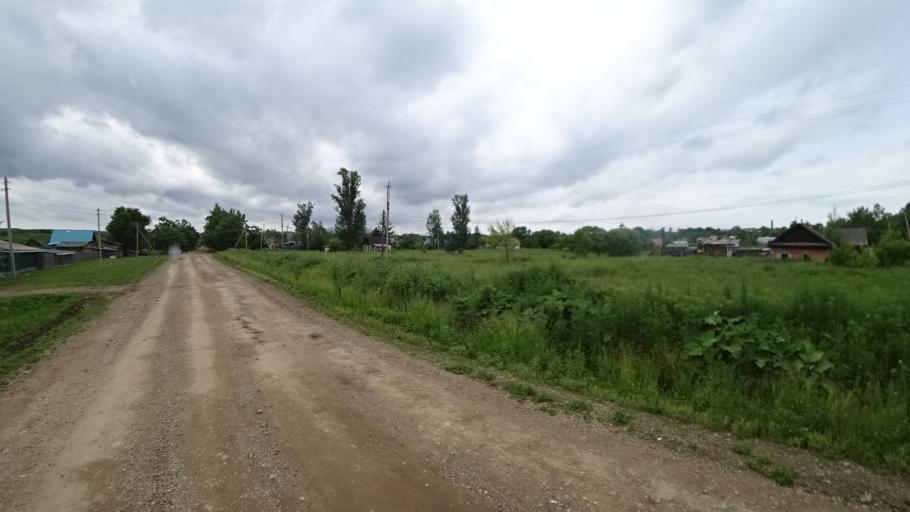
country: RU
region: Primorskiy
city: Novosysoyevka
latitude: 44.2309
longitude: 133.3719
